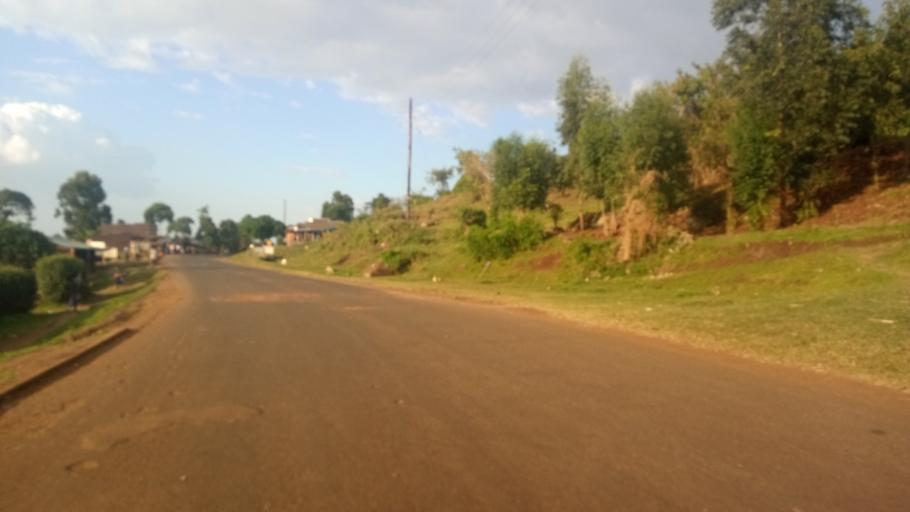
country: UG
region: Eastern Region
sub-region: Kapchorwa District
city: Kapchorwa
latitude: 1.3381
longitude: 34.3591
